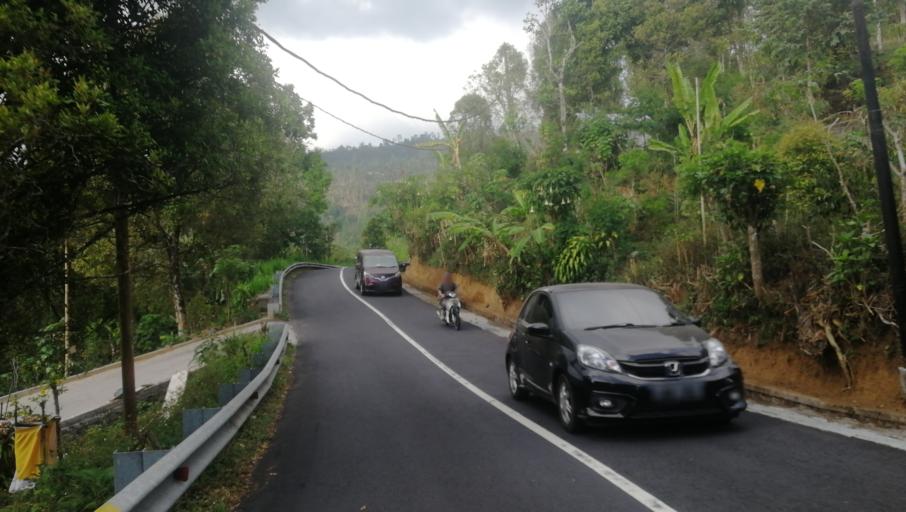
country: ID
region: Bali
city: Munduk
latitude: -8.2573
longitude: 115.0752
